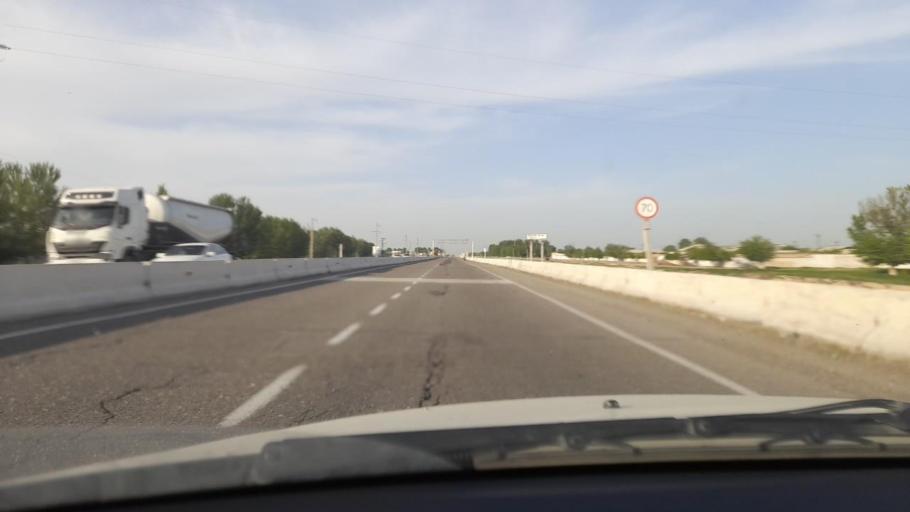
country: UZ
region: Jizzax
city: Paxtakor
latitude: 40.3101
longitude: 68.0833
